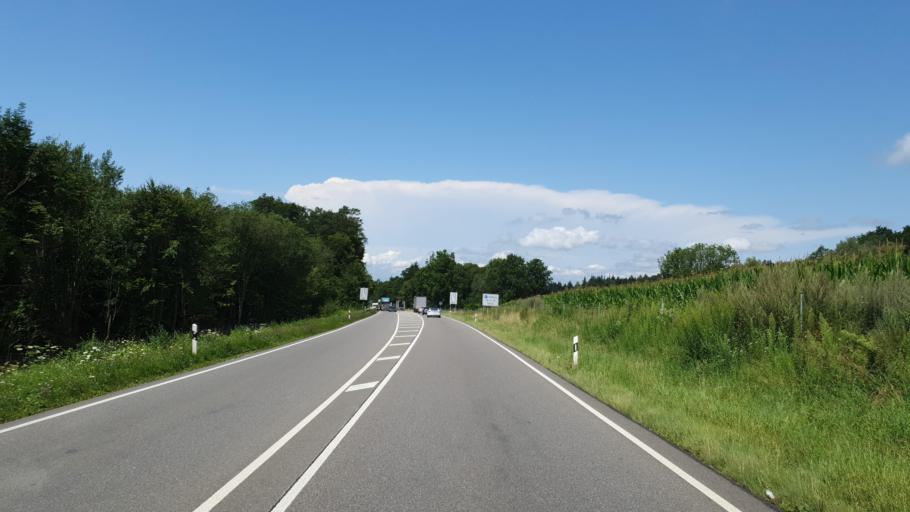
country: DE
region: Baden-Wuerttemberg
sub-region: Tuebingen Region
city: Daisendorf
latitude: 47.7156
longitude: 9.2533
